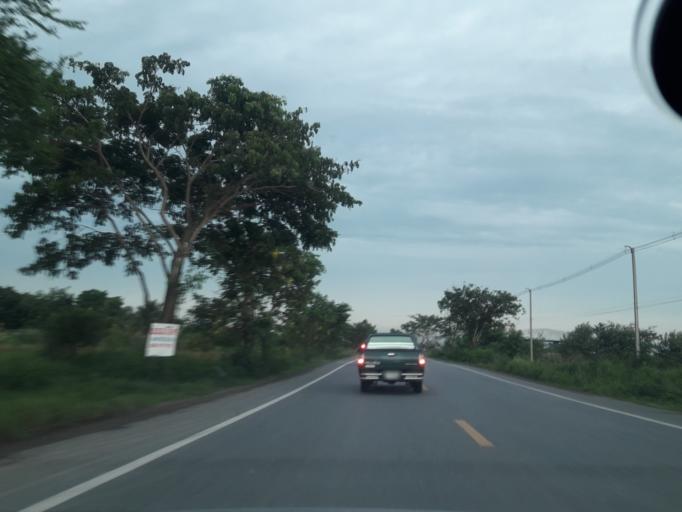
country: TH
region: Phra Nakhon Si Ayutthaya
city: Wang Noi
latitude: 14.1666
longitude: 100.7474
